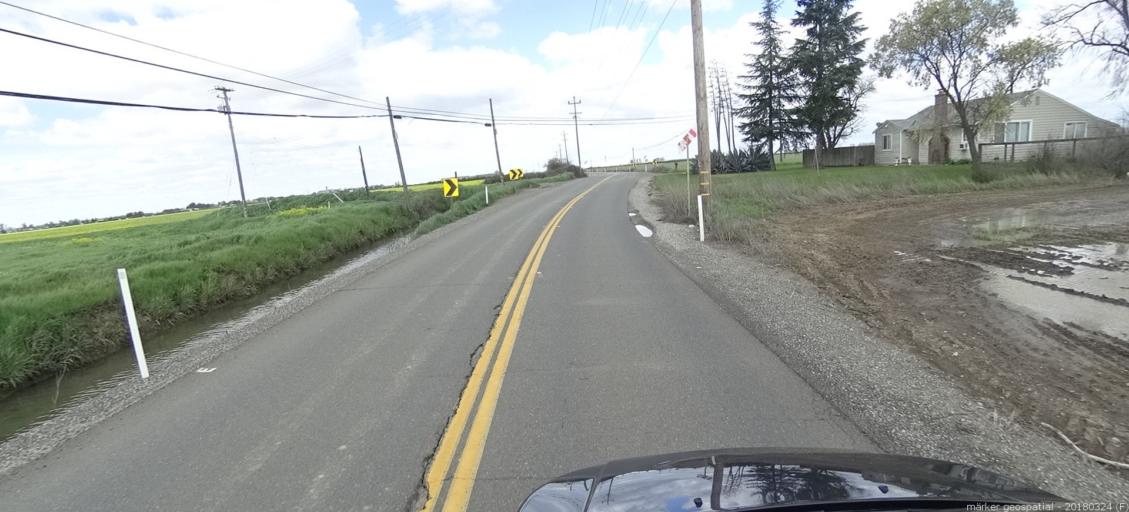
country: US
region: California
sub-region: Yolo County
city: West Sacramento
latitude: 38.6627
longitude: -121.5766
